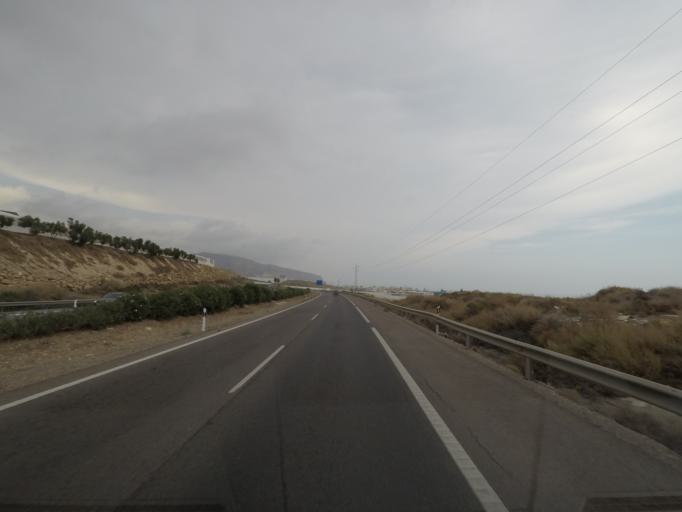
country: ES
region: Andalusia
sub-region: Provincia de Almeria
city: Vicar
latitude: 36.8124
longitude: -2.6153
